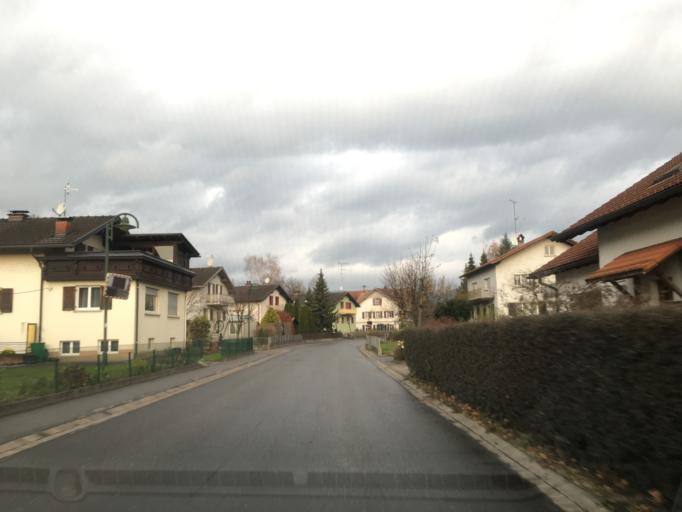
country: AT
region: Vorarlberg
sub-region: Politischer Bezirk Feldkirch
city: Mader
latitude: 47.3440
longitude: 9.6232
